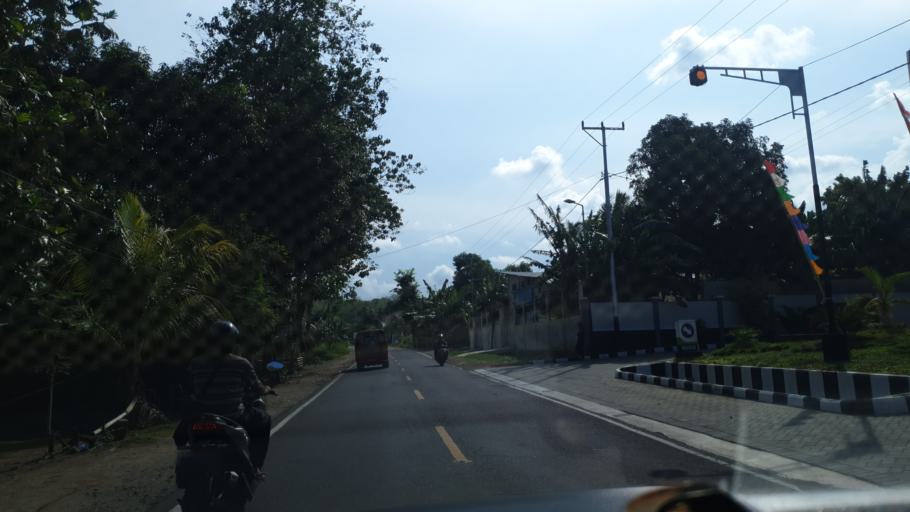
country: ID
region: East Nusa Tenggara
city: Nangalimang
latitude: -8.6395
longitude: 122.2077
